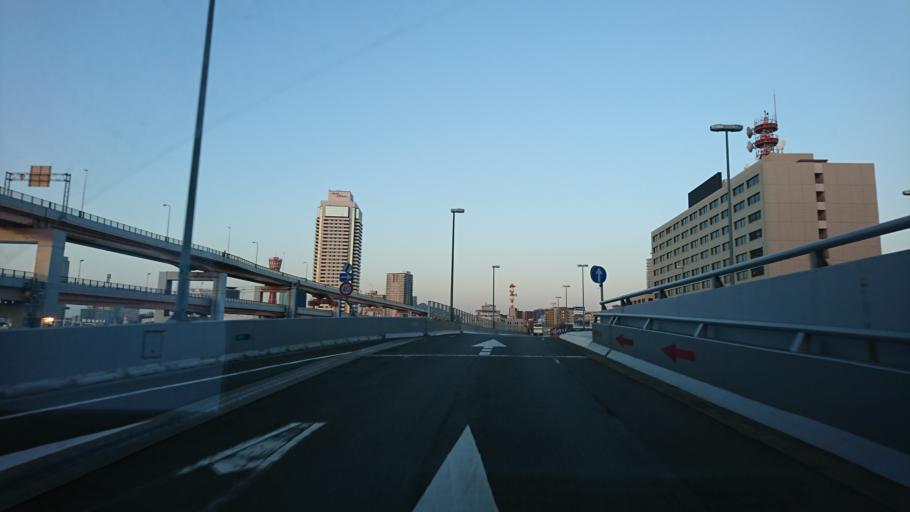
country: JP
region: Hyogo
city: Kobe
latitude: 34.6853
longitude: 135.1940
